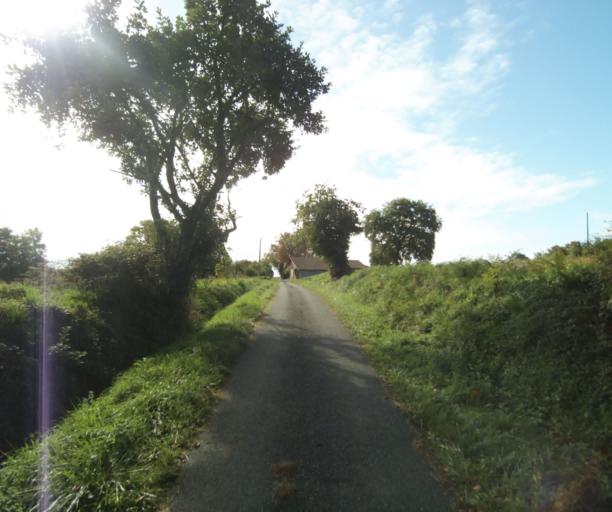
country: FR
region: Midi-Pyrenees
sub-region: Departement du Gers
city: Cazaubon
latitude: 43.8488
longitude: -0.0457
